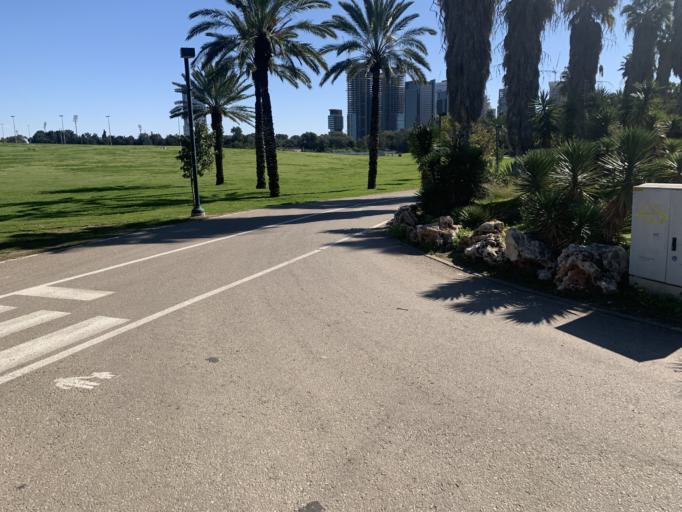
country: IL
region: Tel Aviv
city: Ramat Gan
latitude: 32.1015
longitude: 34.8139
